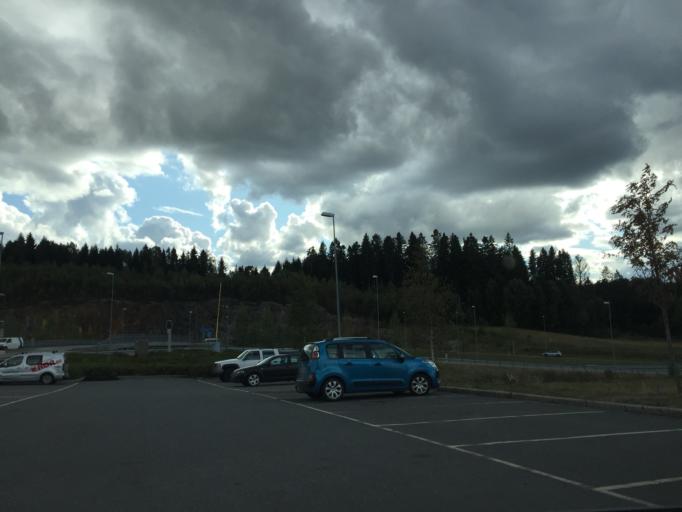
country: NO
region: Ostfold
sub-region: Askim
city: Askim
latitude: 59.5865
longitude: 11.1184
